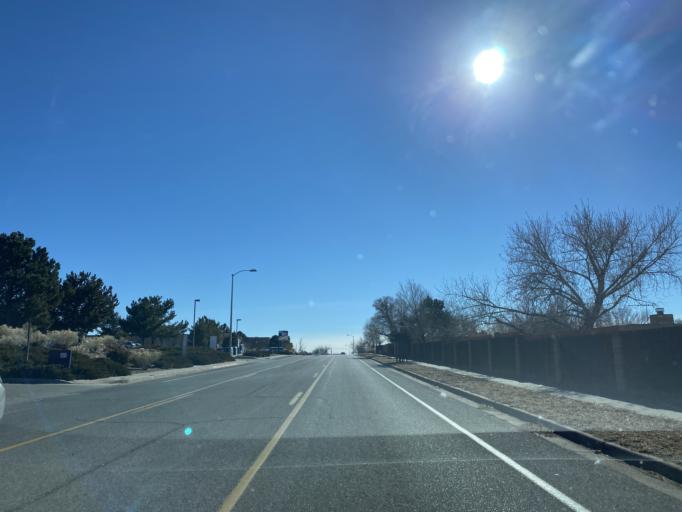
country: US
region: New Mexico
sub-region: Santa Fe County
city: Santa Fe
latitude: 35.6552
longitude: -105.9586
